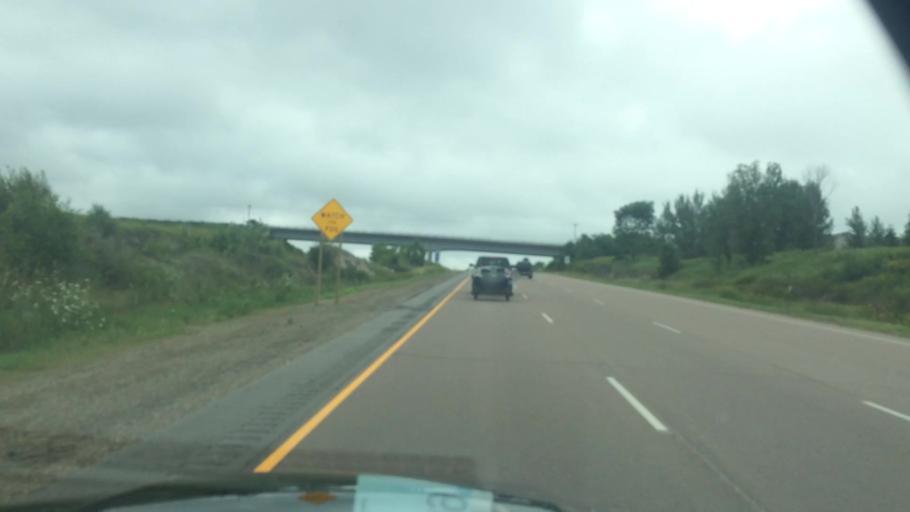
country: US
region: Wisconsin
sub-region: Marathon County
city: Wausau
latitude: 45.0194
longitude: -89.6689
